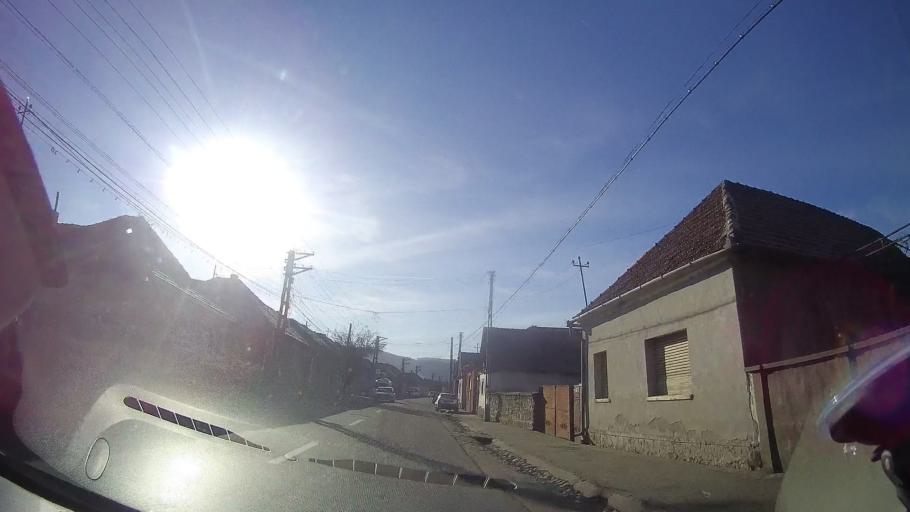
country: RO
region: Bihor
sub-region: Comuna Vadu Crisului
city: Vadu Crisului
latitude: 46.9884
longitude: 22.5186
